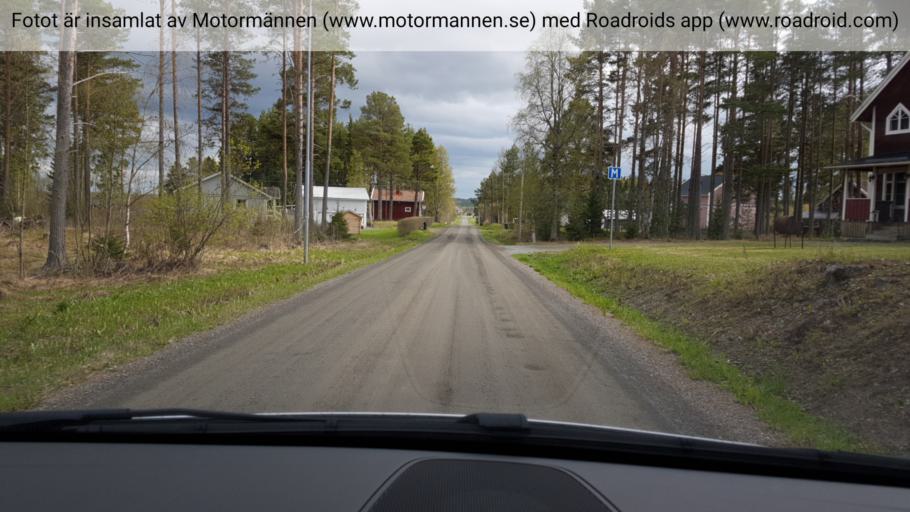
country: SE
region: Jaemtland
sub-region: OEstersunds Kommun
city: Brunflo
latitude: 62.9925
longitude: 14.8076
